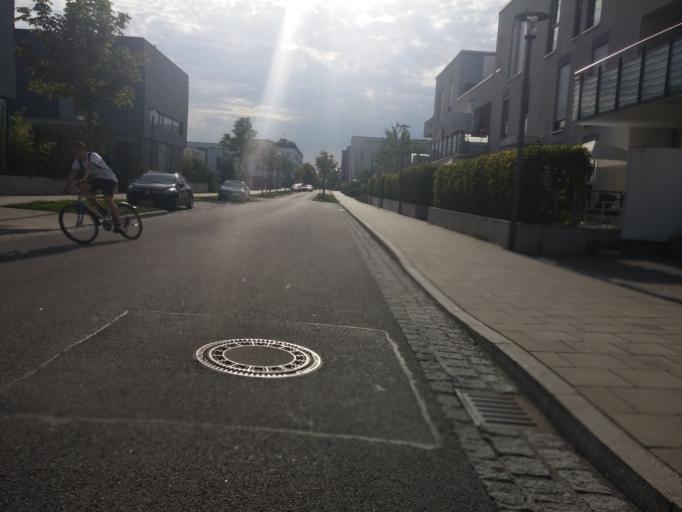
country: DE
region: Bavaria
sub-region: Upper Bavaria
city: Haar
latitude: 48.1296
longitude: 11.6997
